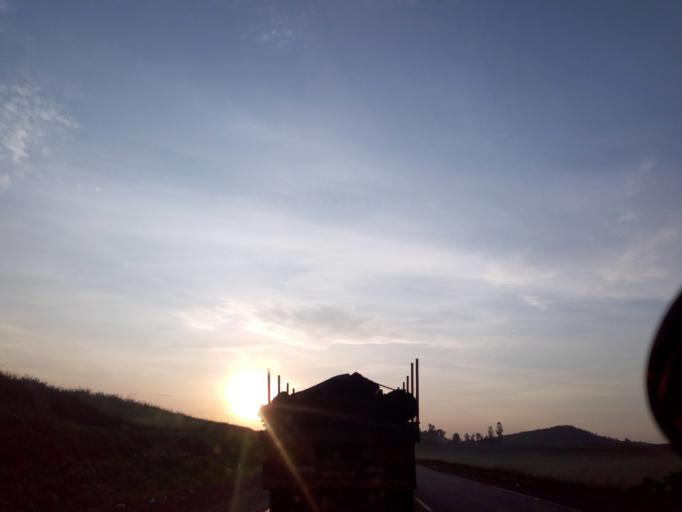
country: UG
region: Central Region
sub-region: Buikwe District
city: Njeru
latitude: 0.4070
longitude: 33.0816
